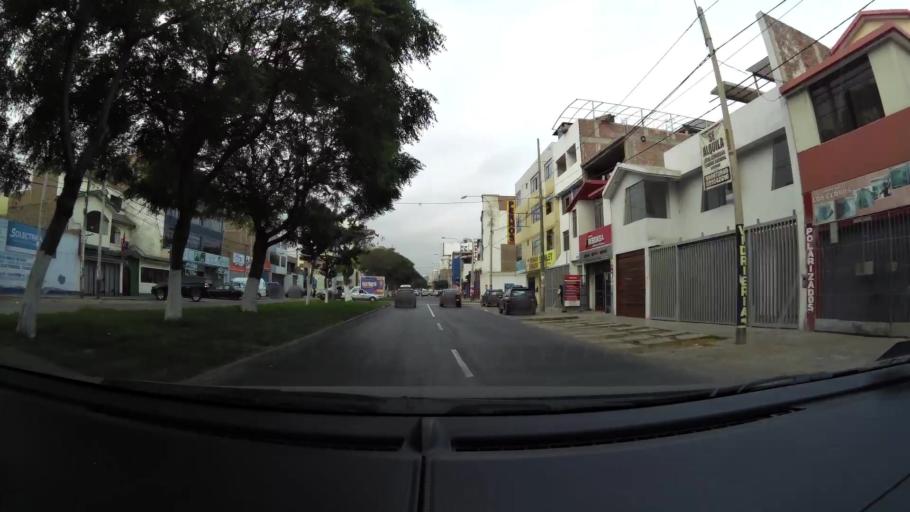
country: PE
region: La Libertad
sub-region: Provincia de Trujillo
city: La Esperanza
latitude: -8.0971
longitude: -79.0426
